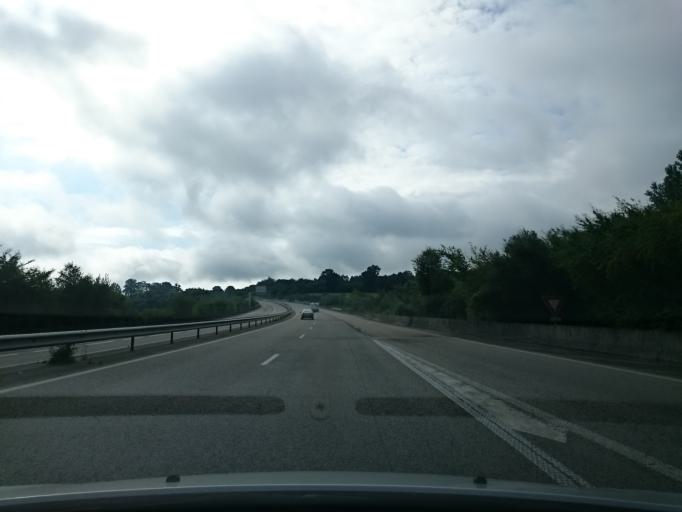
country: FR
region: Lower Normandy
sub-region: Departement du Calvados
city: Saint-Desir
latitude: 49.1267
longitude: 0.1920
